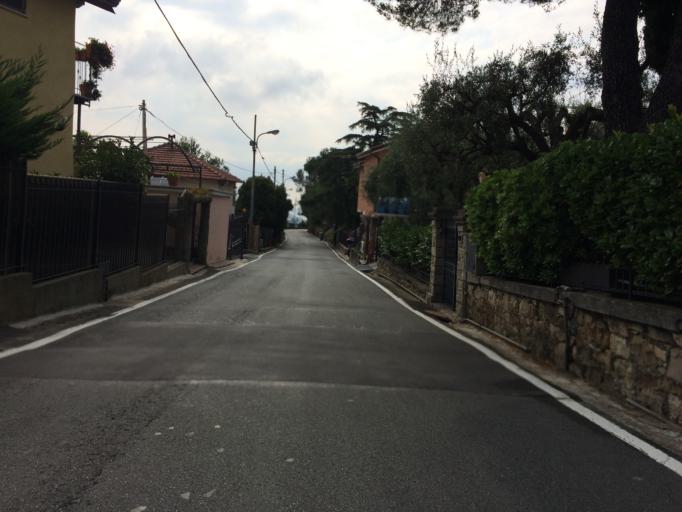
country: IT
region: Liguria
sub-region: Provincia di Imperia
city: San Remo
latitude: 43.8315
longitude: 7.7618
